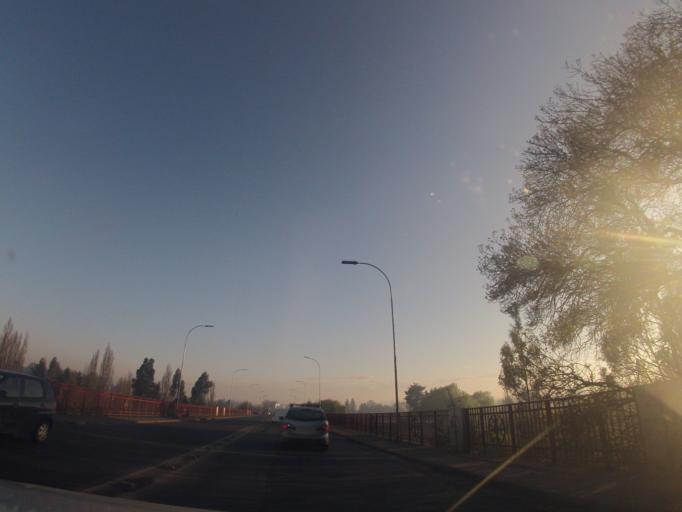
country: CL
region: Araucania
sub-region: Provincia de Cautin
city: Temuco
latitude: -38.7563
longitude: -72.6092
